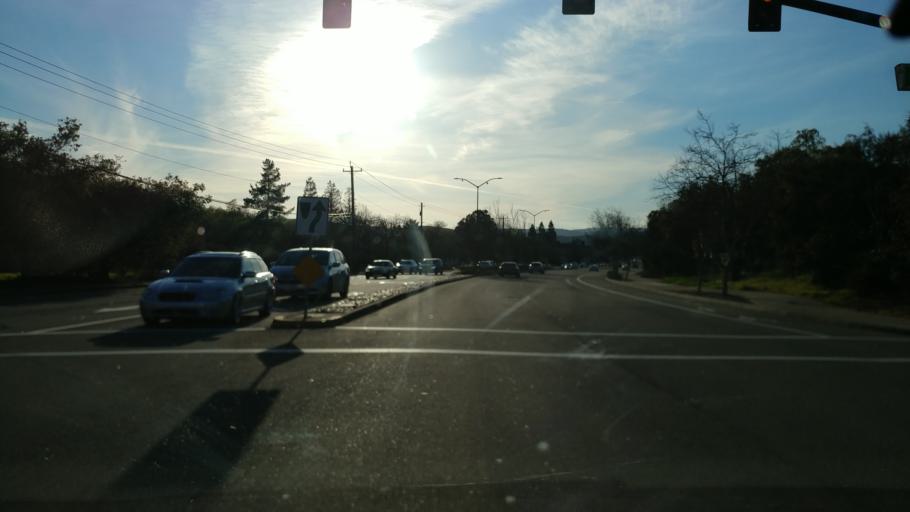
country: US
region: California
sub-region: Contra Costa County
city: Blackhawk
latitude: 37.7985
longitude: -121.9129
